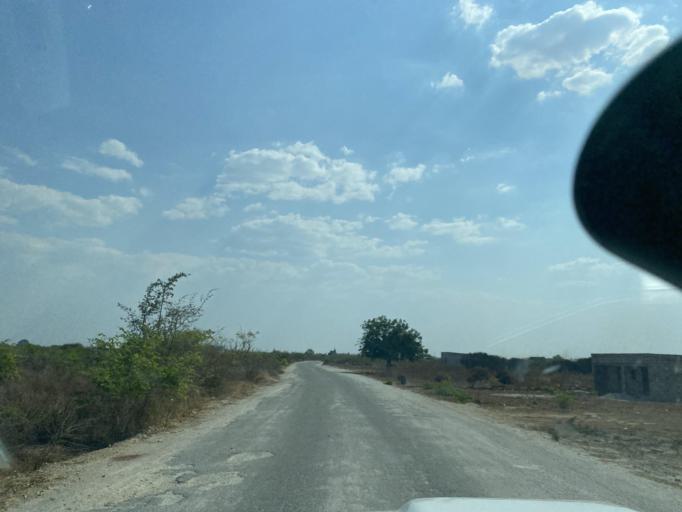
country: ZM
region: Lusaka
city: Lusaka
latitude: -15.3708
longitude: 28.0798
